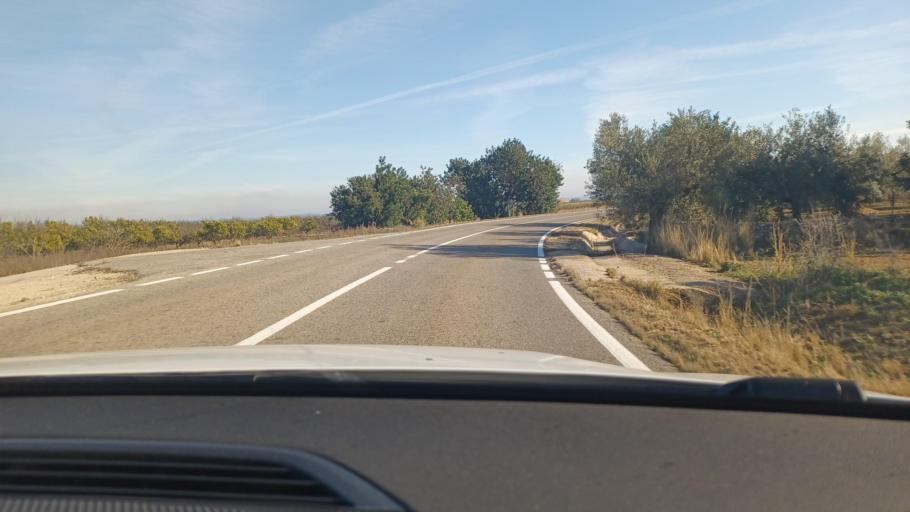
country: ES
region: Catalonia
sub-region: Provincia de Tarragona
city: Santa Barbara
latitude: 40.7216
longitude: 0.4449
